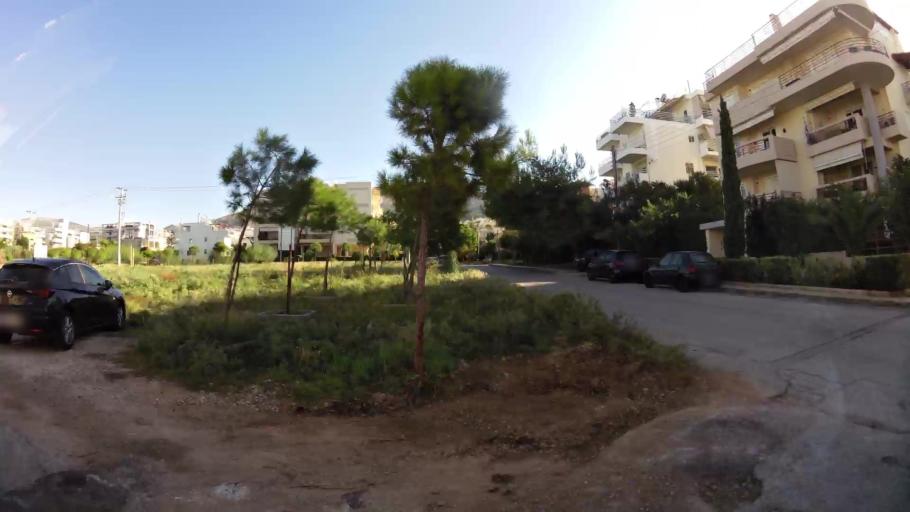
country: GR
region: Attica
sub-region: Nomarchia Athinas
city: Glyfada
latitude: 37.8664
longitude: 23.7627
